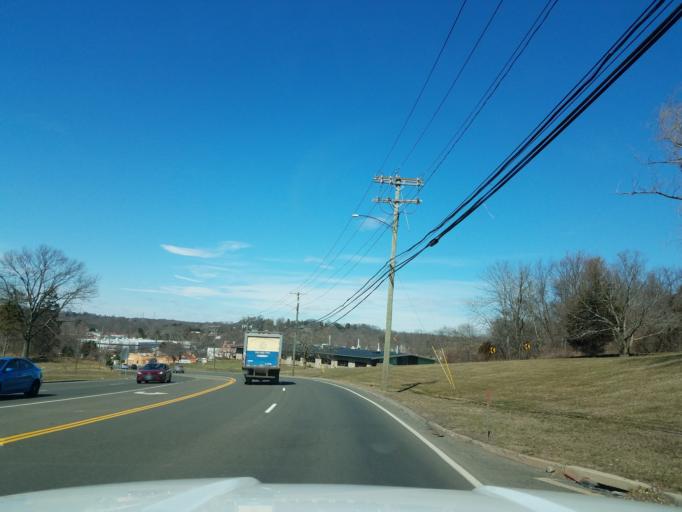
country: US
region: Connecticut
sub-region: New Haven County
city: Woodmont
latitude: 41.2583
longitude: -73.0003
